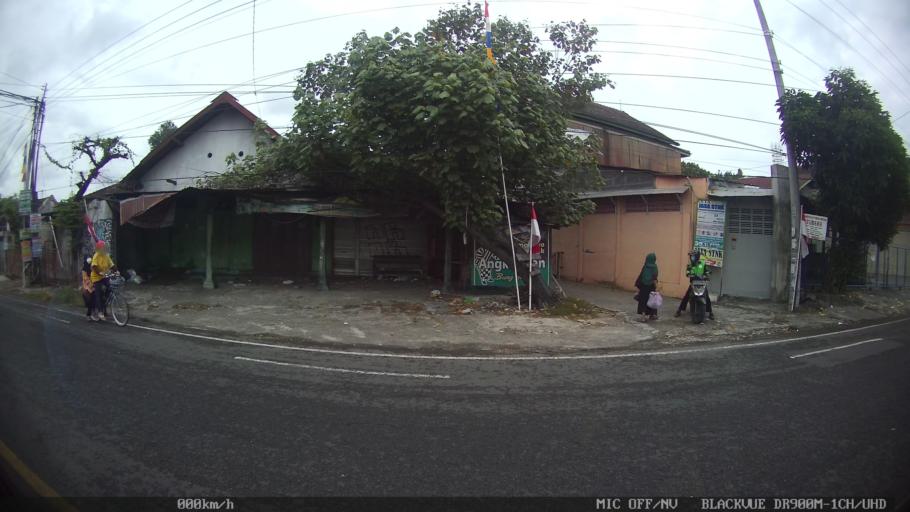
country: ID
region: Daerah Istimewa Yogyakarta
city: Depok
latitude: -7.8115
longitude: 110.4085
